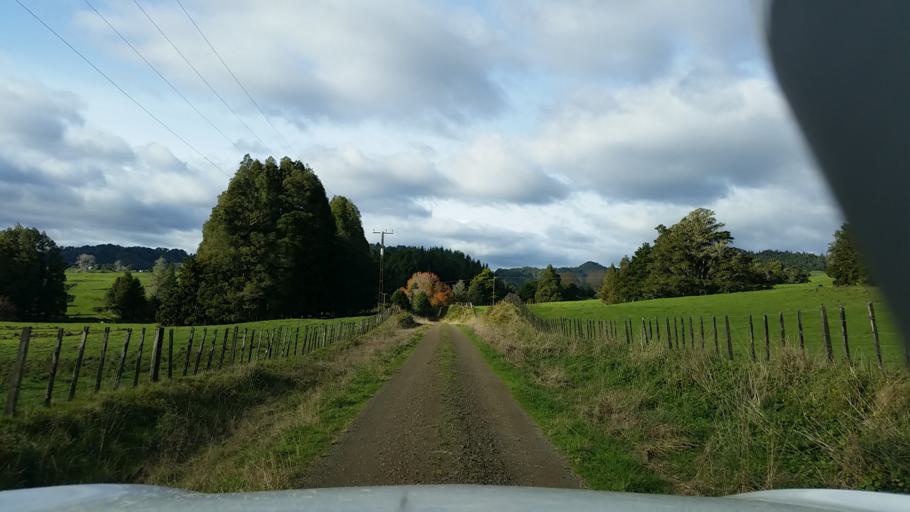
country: NZ
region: Taranaki
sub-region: New Plymouth District
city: Waitara
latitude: -38.9742
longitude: 174.5569
